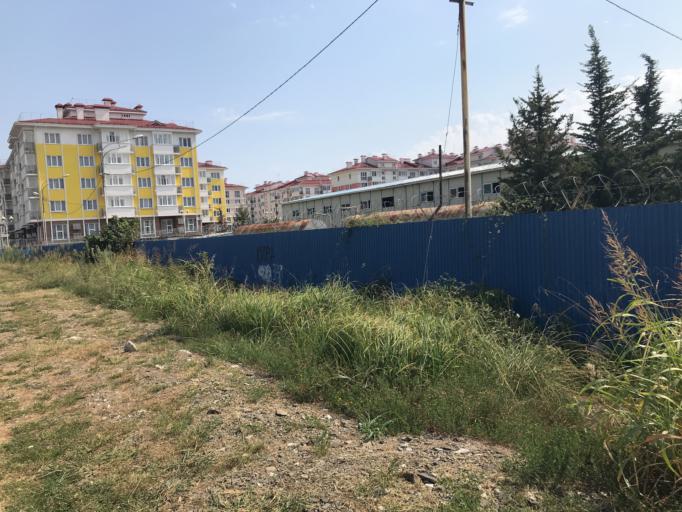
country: RU
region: Krasnodarskiy
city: Vysokoye
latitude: 43.4044
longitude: 39.9823
